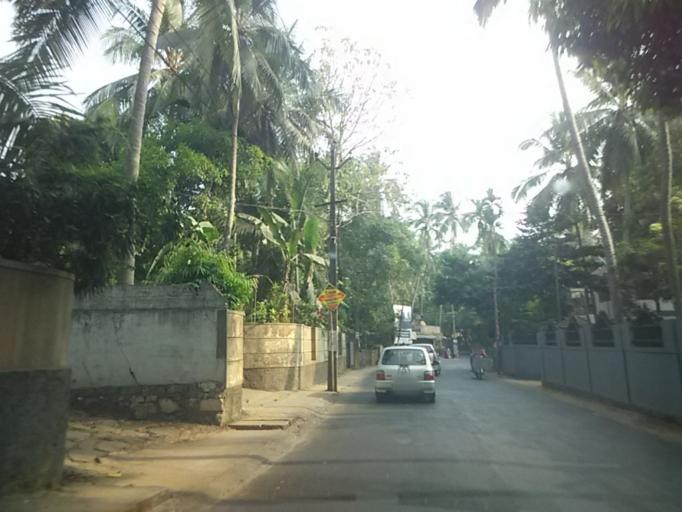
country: IN
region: Kerala
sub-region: Kozhikode
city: Kozhikode
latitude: 11.3512
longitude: 75.7618
